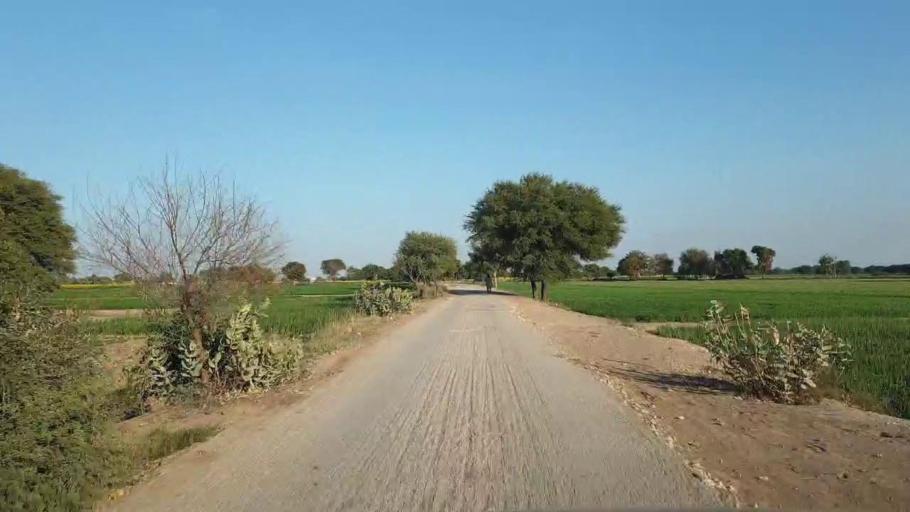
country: PK
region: Sindh
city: Shahpur Chakar
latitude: 26.1284
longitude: 68.5492
